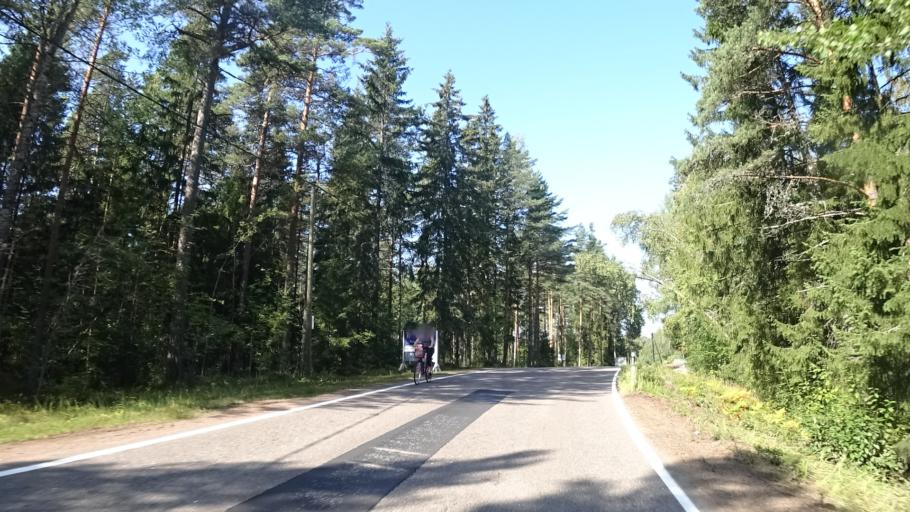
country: FI
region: Kymenlaakso
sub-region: Kotka-Hamina
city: Hamina
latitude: 60.5545
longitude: 27.2393
